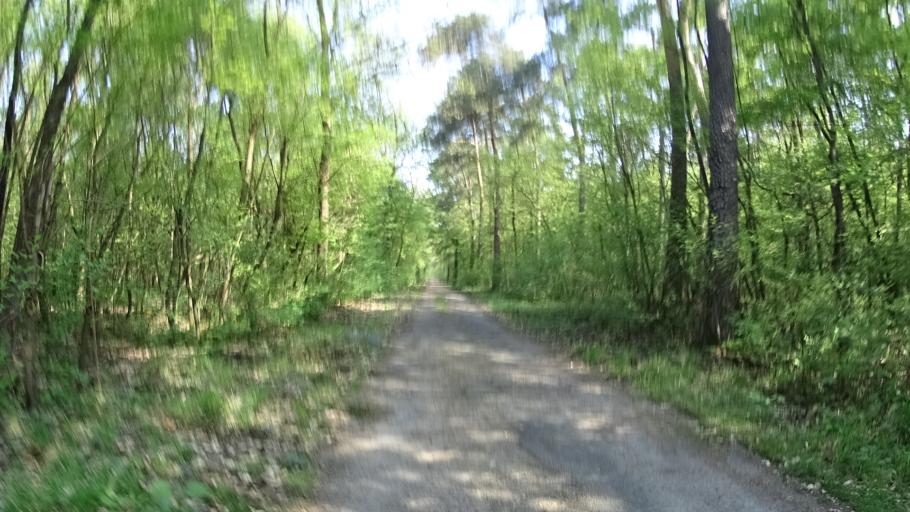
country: DE
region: Hesse
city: Viernheim
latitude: 49.5403
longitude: 8.5237
